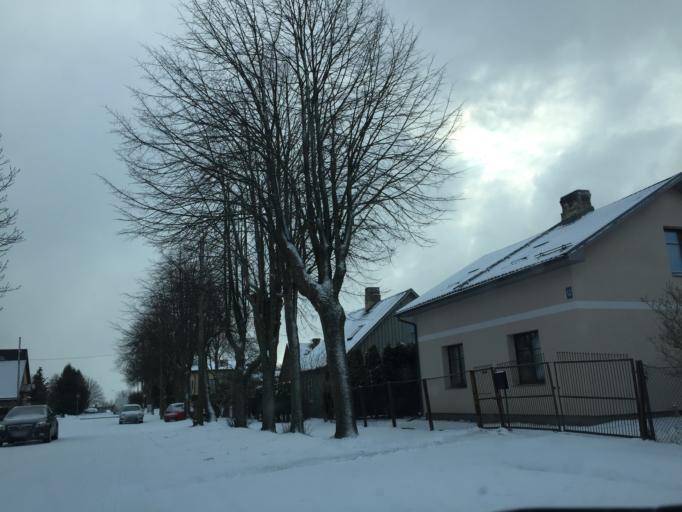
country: LV
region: Ventspils
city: Ventspils
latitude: 57.3797
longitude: 21.5613
